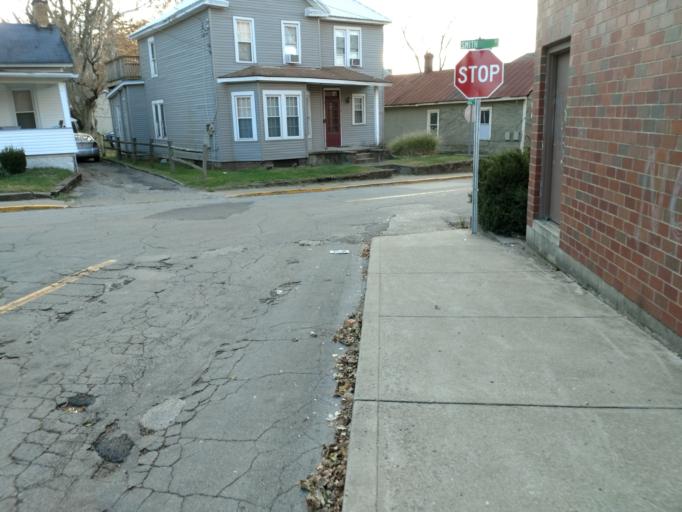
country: US
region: Ohio
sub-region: Athens County
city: Athens
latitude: 39.3304
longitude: -82.1074
